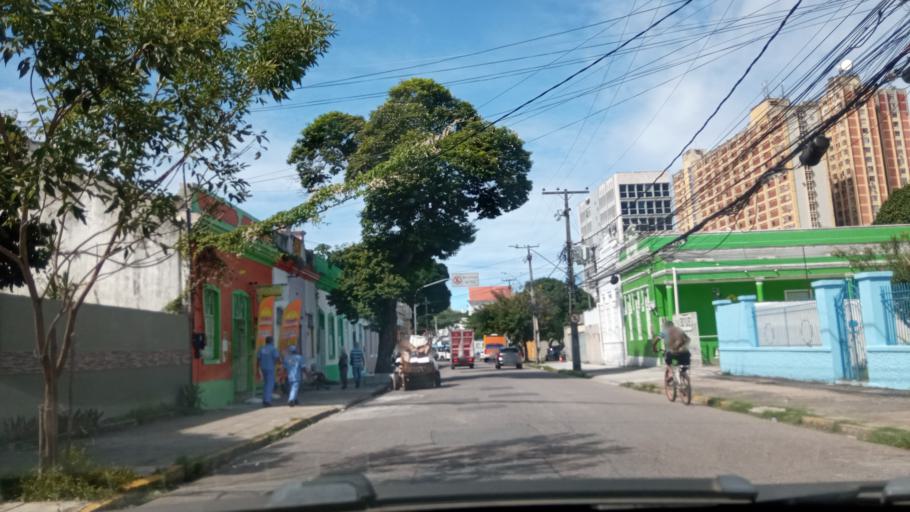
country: BR
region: Pernambuco
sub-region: Recife
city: Recife
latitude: -8.0586
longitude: -34.8960
